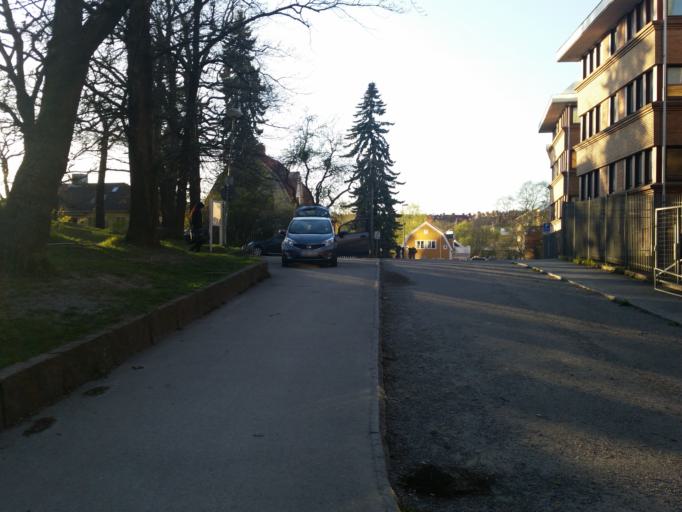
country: SE
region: Stockholm
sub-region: Solna Kommun
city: Solna
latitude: 59.3621
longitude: 17.9954
